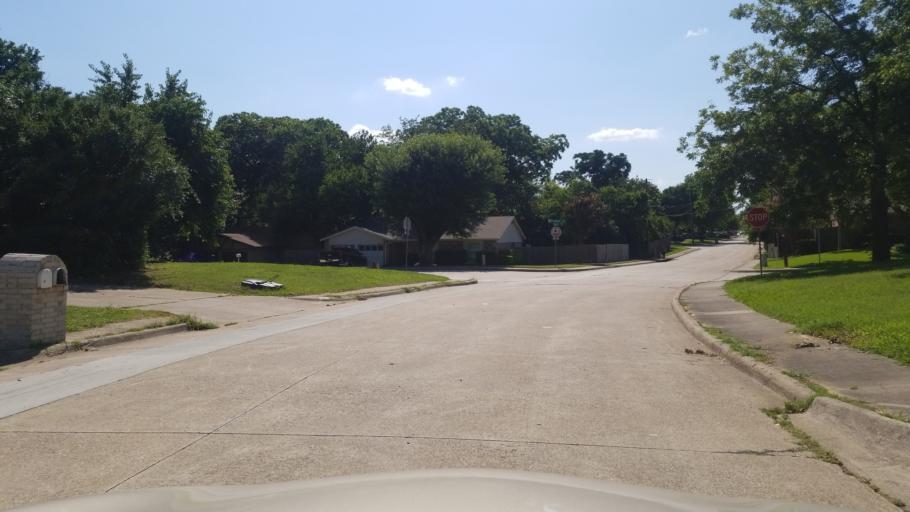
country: US
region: Texas
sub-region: Dallas County
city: Grand Prairie
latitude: 32.6786
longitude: -97.0143
